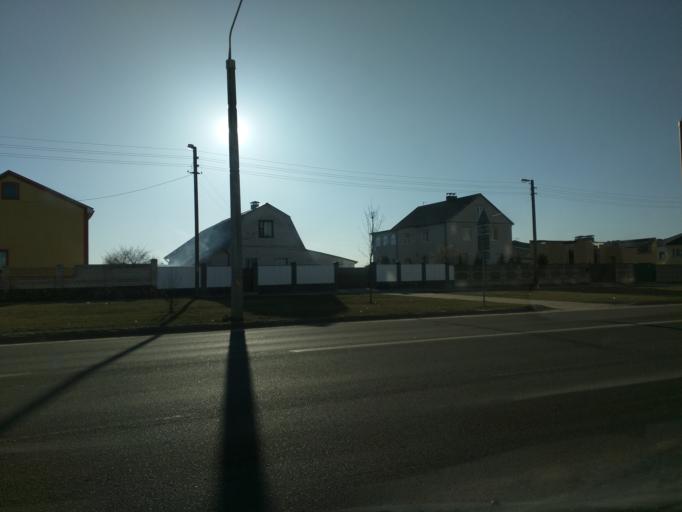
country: BY
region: Mogilev
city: Babruysk
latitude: 53.1653
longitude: 29.1655
